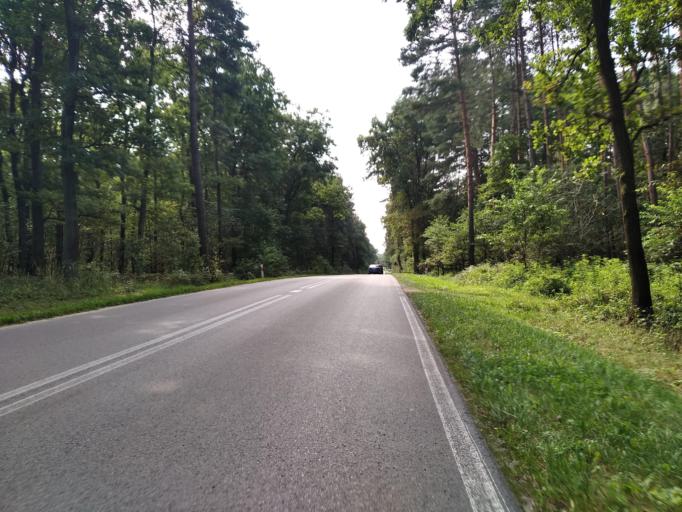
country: PL
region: Subcarpathian Voivodeship
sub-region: Powiat ropczycko-sedziszowski
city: Ostrow
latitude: 50.1257
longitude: 21.5868
